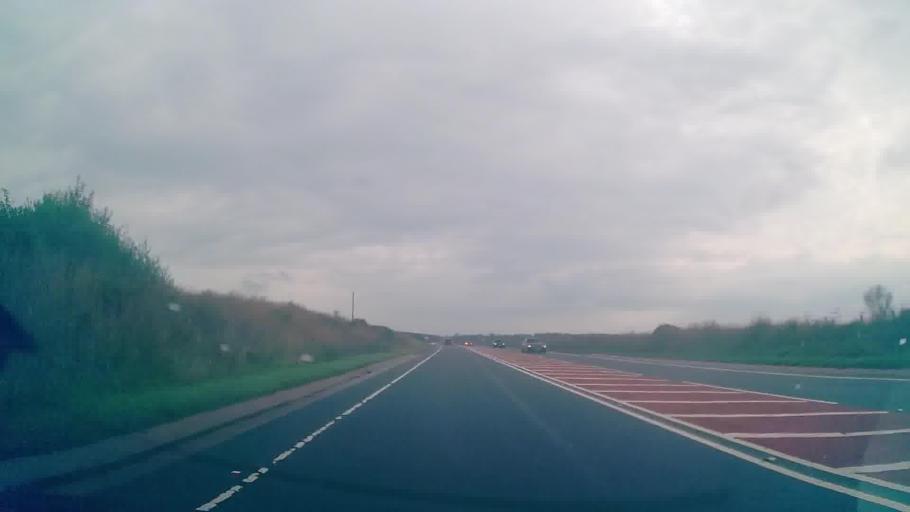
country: GB
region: Scotland
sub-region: Dumfries and Galloway
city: Lockerbie
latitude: 55.0204
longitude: -3.3693
